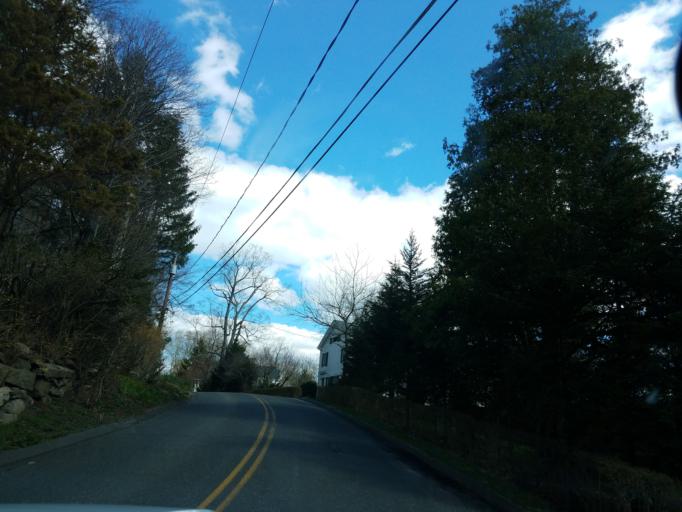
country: US
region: Connecticut
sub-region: Litchfield County
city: Watertown
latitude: 41.6125
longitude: -73.1191
